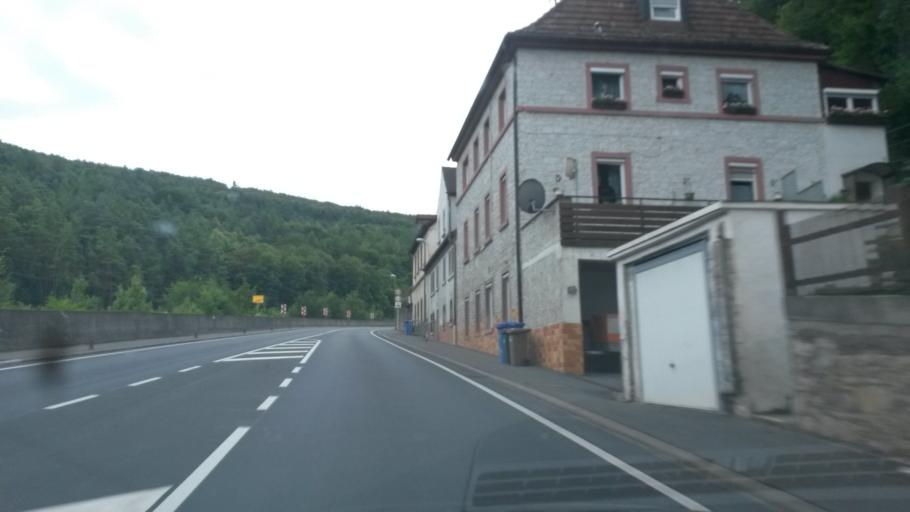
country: DE
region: Bavaria
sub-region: Regierungsbezirk Unterfranken
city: Zell am Main
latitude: 49.7988
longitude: 9.8757
